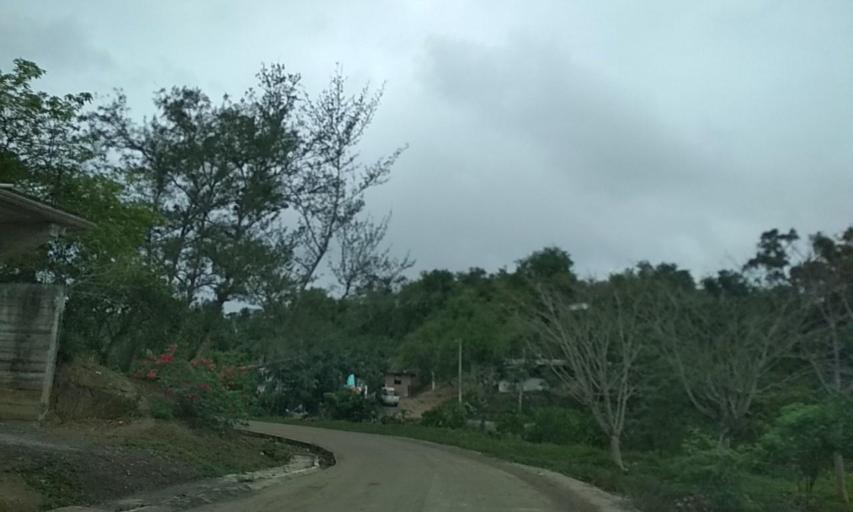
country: MX
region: Veracruz
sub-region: Papantla
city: El Chote
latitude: 20.3837
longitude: -97.3522
